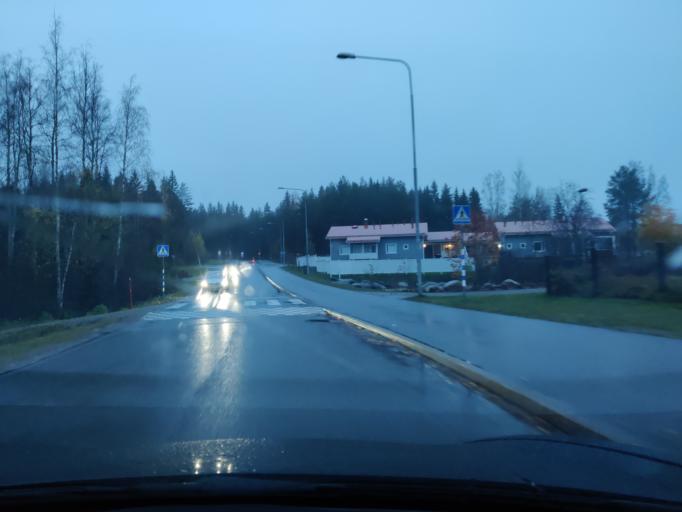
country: FI
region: Northern Savo
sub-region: Kuopio
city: Kuopio
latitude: 62.8316
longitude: 27.7152
